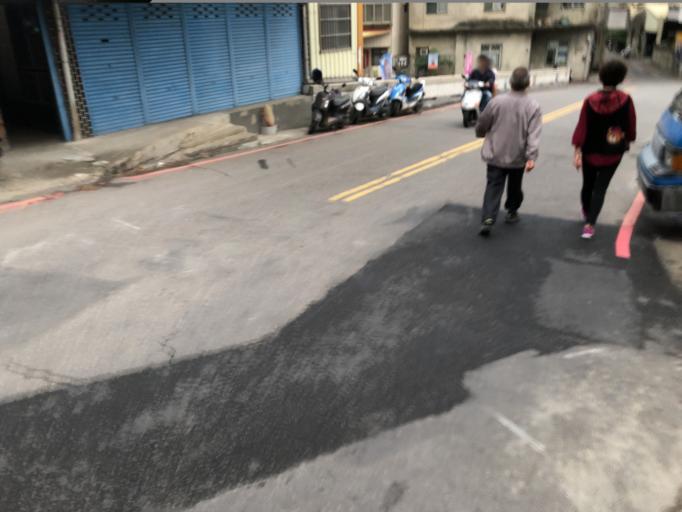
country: TW
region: Taiwan
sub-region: Miaoli
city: Miaoli
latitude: 24.5560
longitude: 120.8202
